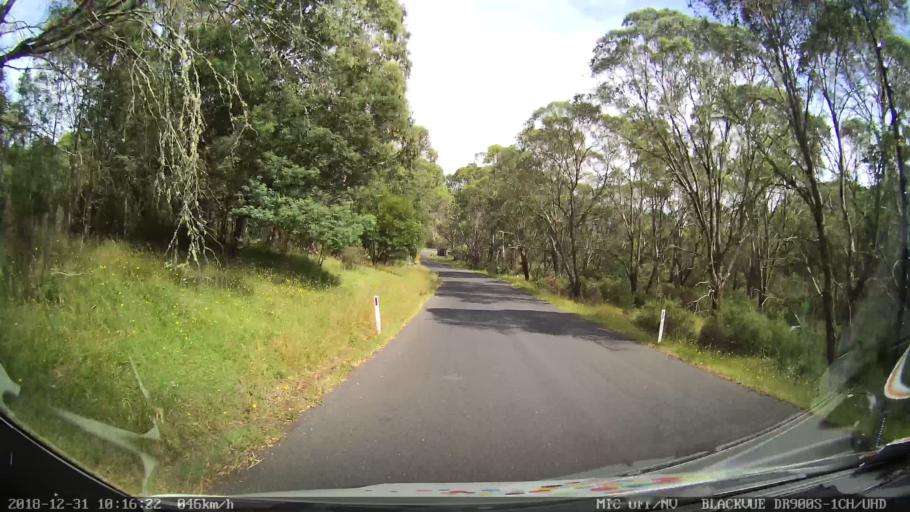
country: AU
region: New South Wales
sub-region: Snowy River
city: Jindabyne
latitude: -36.5394
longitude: 148.1370
